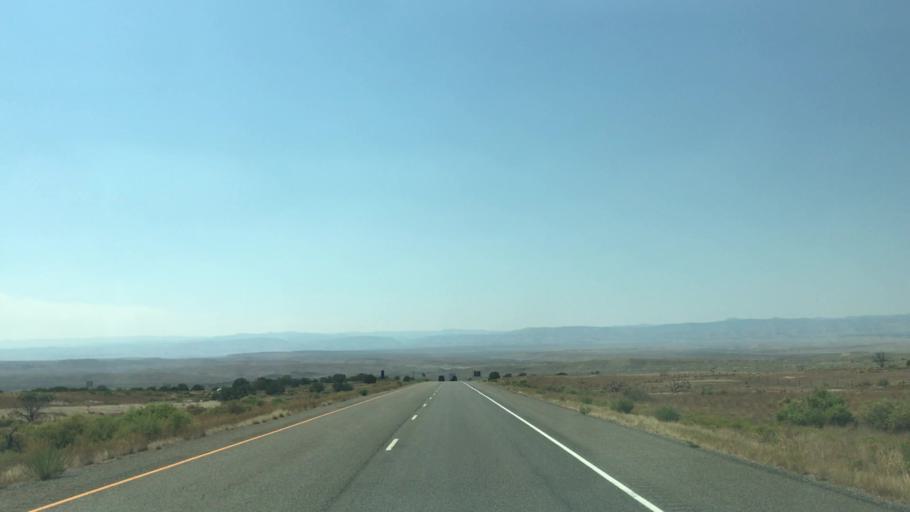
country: US
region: Colorado
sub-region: Mesa County
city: Loma
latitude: 39.1915
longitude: -109.0439
